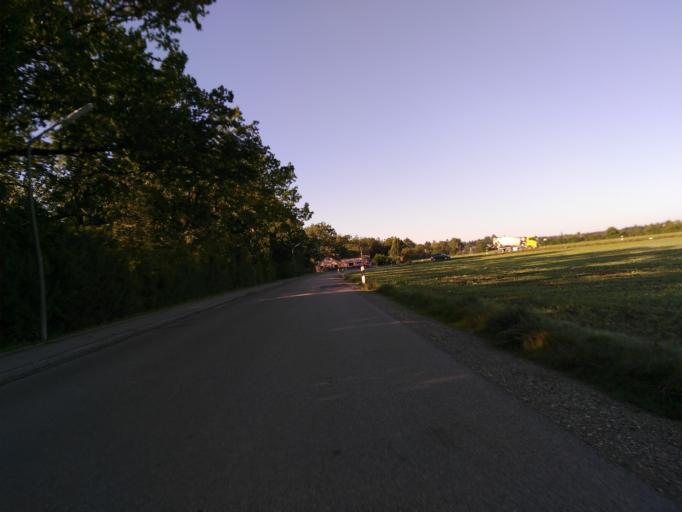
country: DE
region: Bavaria
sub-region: Upper Bavaria
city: Hohenbrunn
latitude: 48.0395
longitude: 11.7135
